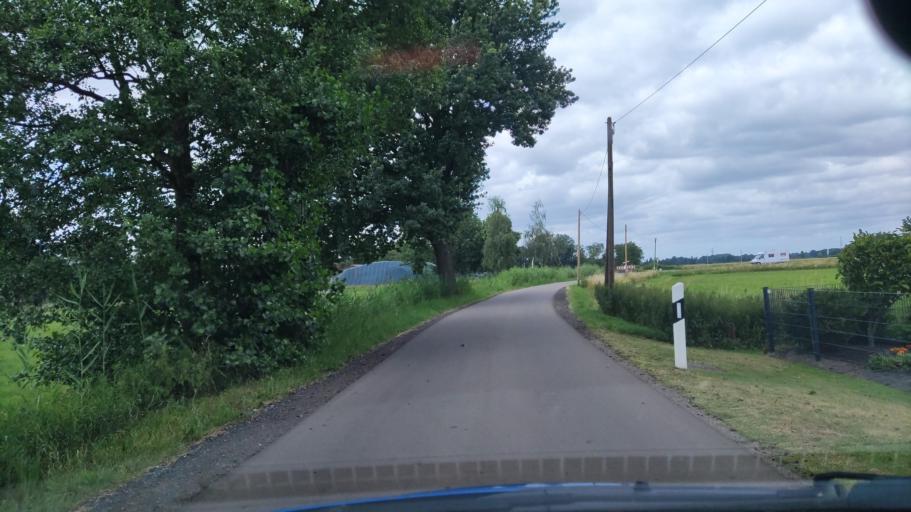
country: DE
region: Lower Saxony
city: Stelle
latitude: 53.4252
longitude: 10.0700
